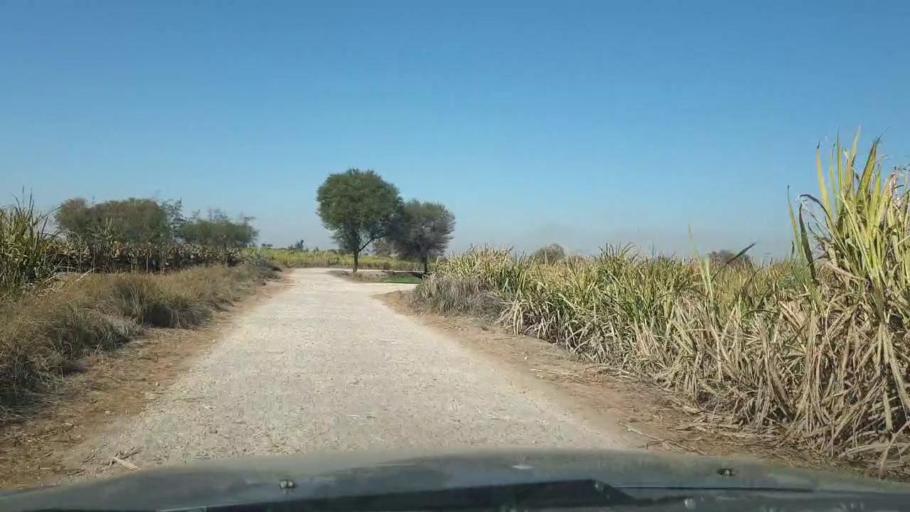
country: PK
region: Sindh
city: Ghotki
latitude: 28.0491
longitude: 69.2412
